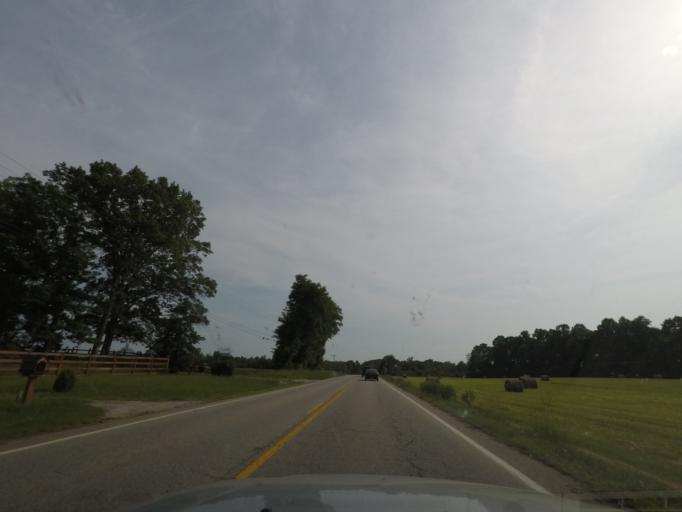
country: US
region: Virginia
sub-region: Prince Edward County
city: Hampden Sydney
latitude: 37.1766
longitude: -78.4362
